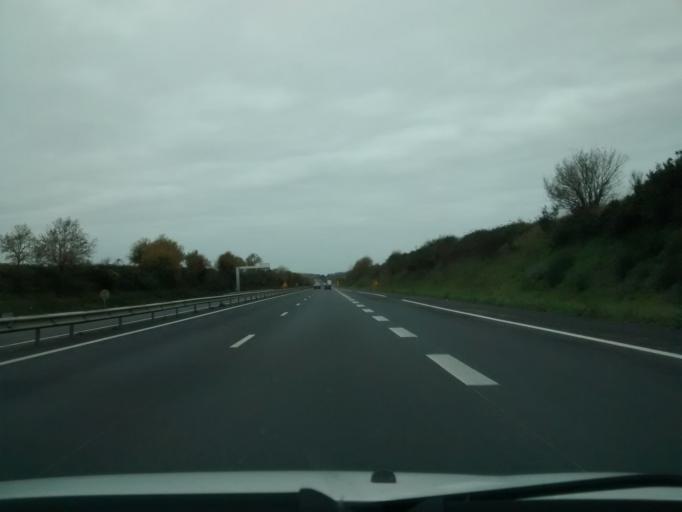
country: FR
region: Brittany
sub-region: Departement d'Ille-et-Vilaine
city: Torce
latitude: 48.0758
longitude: -1.2753
